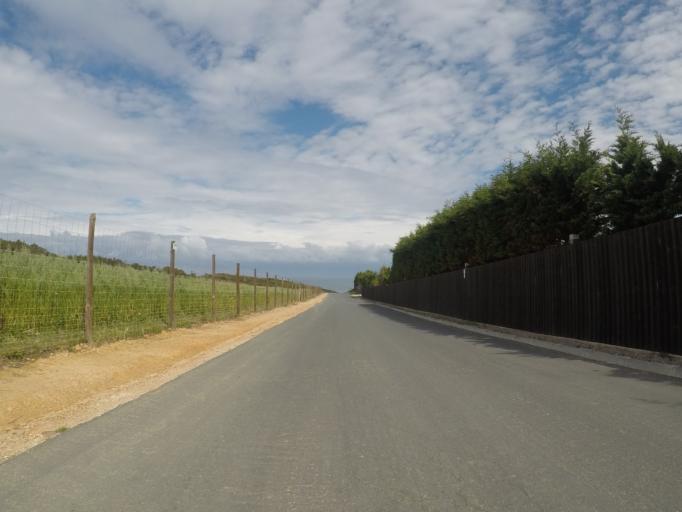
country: PT
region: Beja
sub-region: Odemira
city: Sao Teotonio
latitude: 37.4964
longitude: -8.7895
